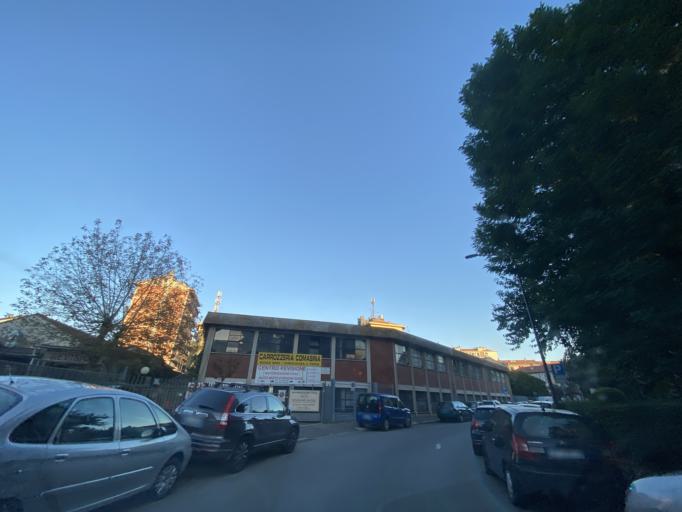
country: IT
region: Lombardy
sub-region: Citta metropolitana di Milano
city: Cormano
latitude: 45.5288
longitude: 9.1599
